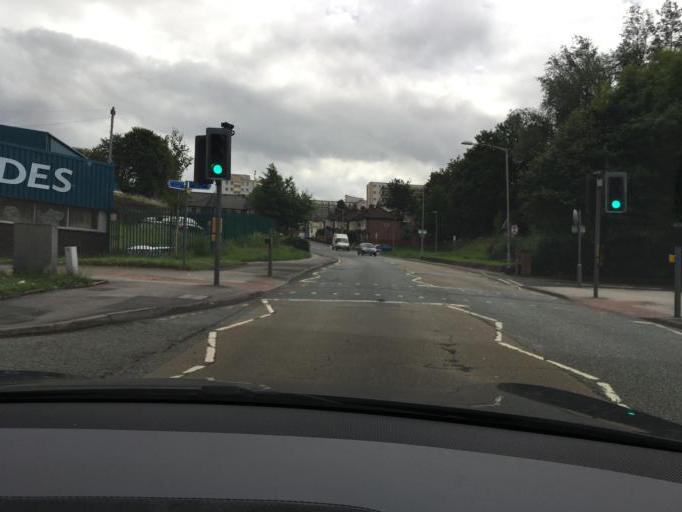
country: GB
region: England
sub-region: Borough of Stockport
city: Stockport
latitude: 53.4059
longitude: -2.1659
